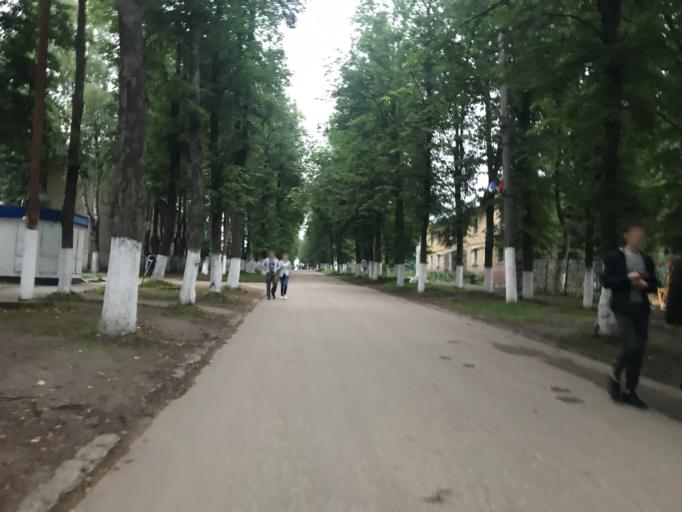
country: RU
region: Tula
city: Priupskiy
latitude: 53.9425
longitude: 37.7014
